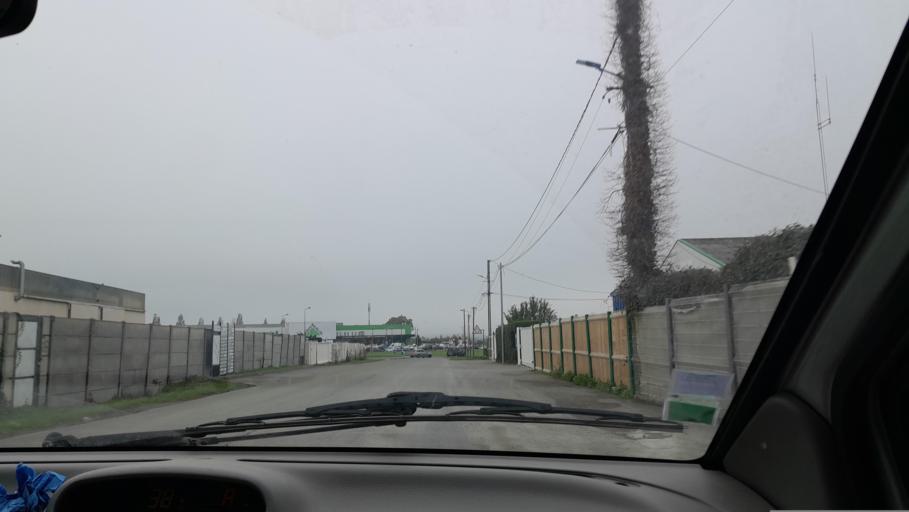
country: FR
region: Pays de la Loire
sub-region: Departement de la Mayenne
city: Saint-Berthevin
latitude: 48.0607
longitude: -0.8096
